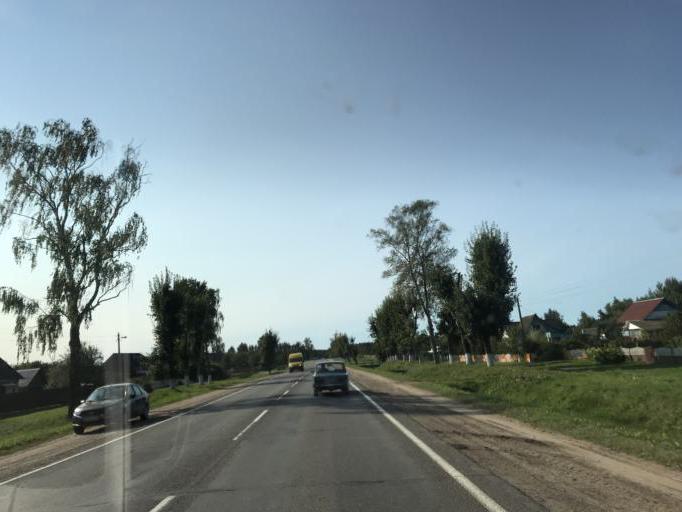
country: BY
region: Mogilev
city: Buynichy
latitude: 53.8285
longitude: 30.2429
